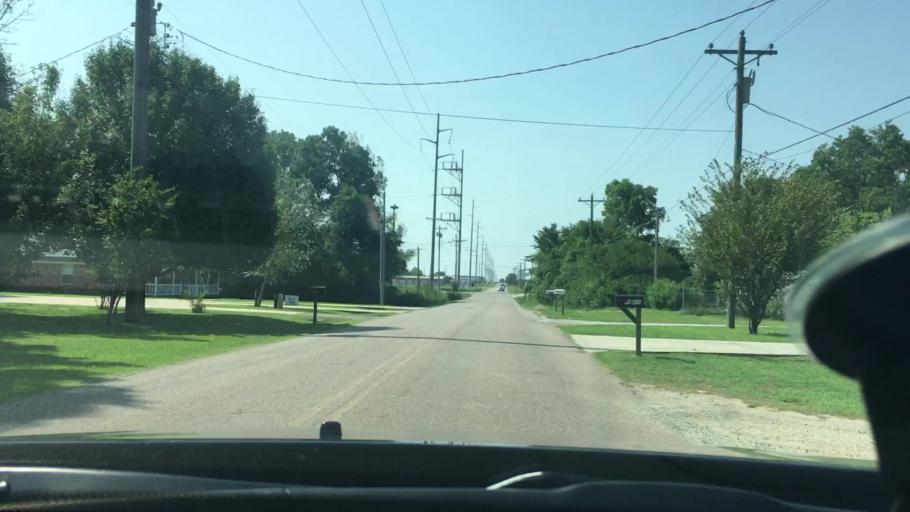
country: US
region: Oklahoma
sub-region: Bryan County
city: Durant
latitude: 34.0068
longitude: -96.4253
